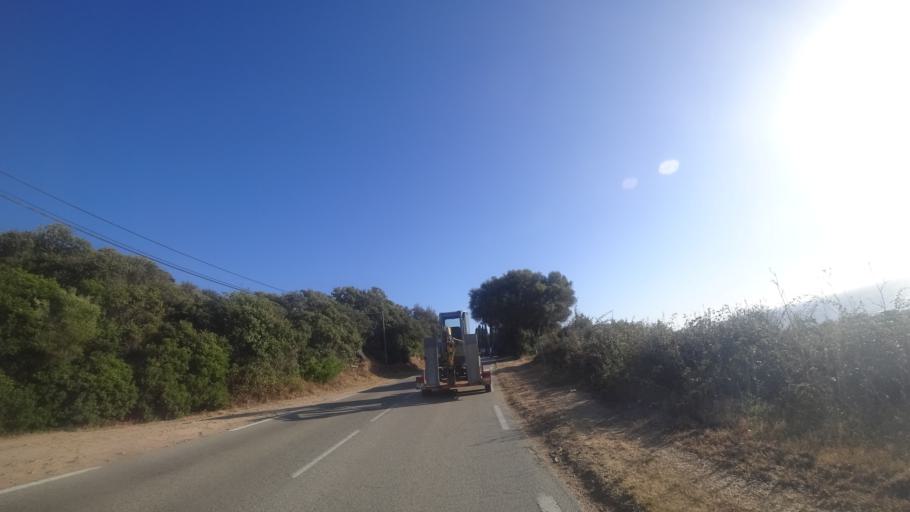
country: FR
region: Corsica
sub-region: Departement de la Corse-du-Sud
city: Cargese
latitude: 42.1455
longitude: 8.6031
